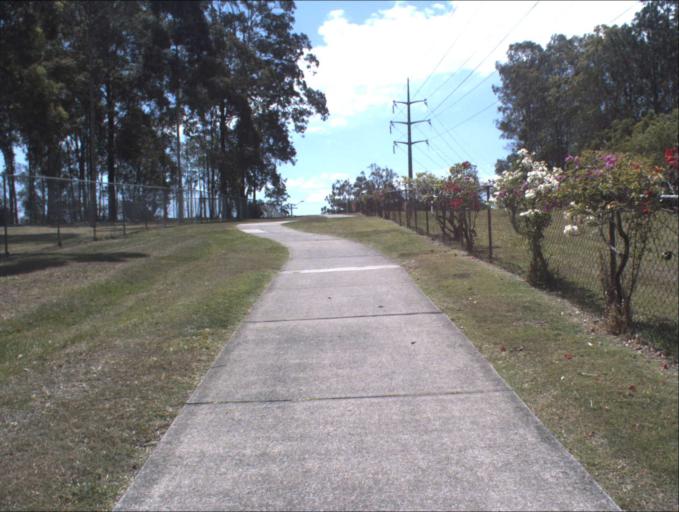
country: AU
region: Queensland
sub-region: Logan
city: Slacks Creek
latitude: -27.6366
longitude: 153.1492
